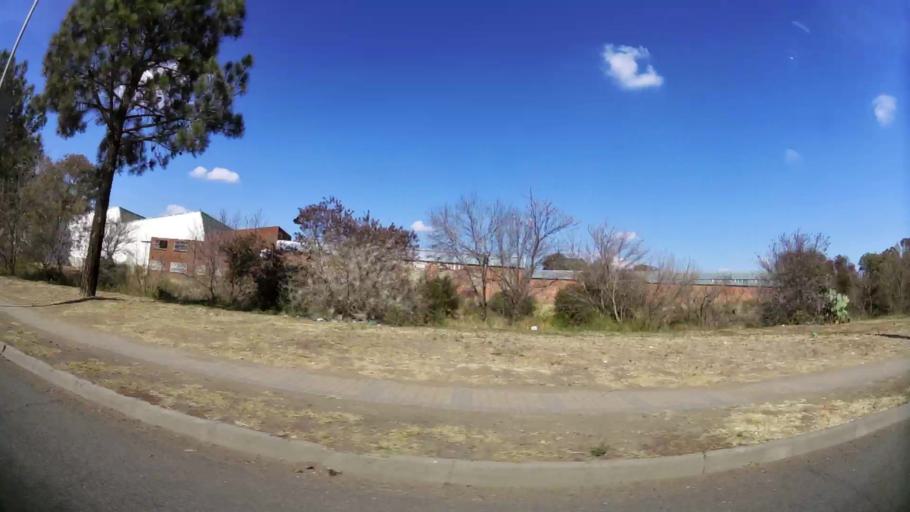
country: ZA
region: Orange Free State
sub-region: Mangaung Metropolitan Municipality
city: Bloemfontein
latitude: -29.1196
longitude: 26.2313
